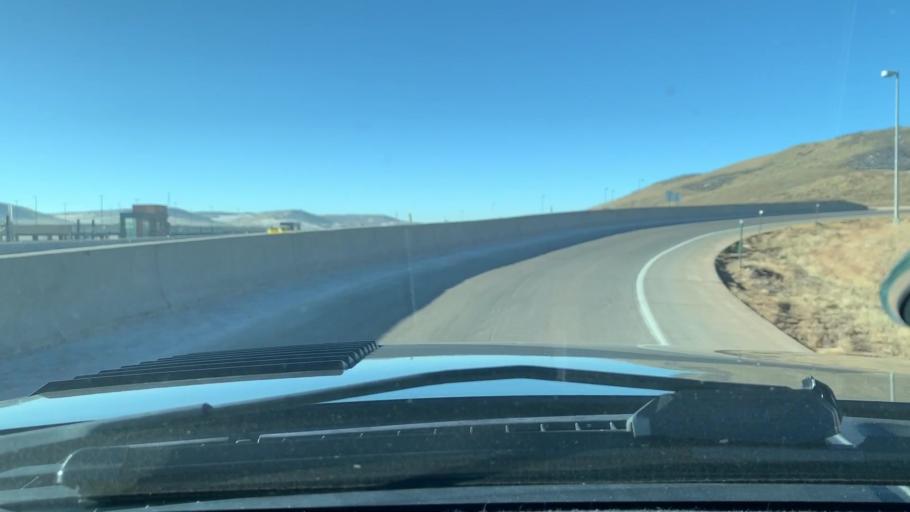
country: US
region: Colorado
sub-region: Douglas County
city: Meridian
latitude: 39.5220
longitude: -104.8653
